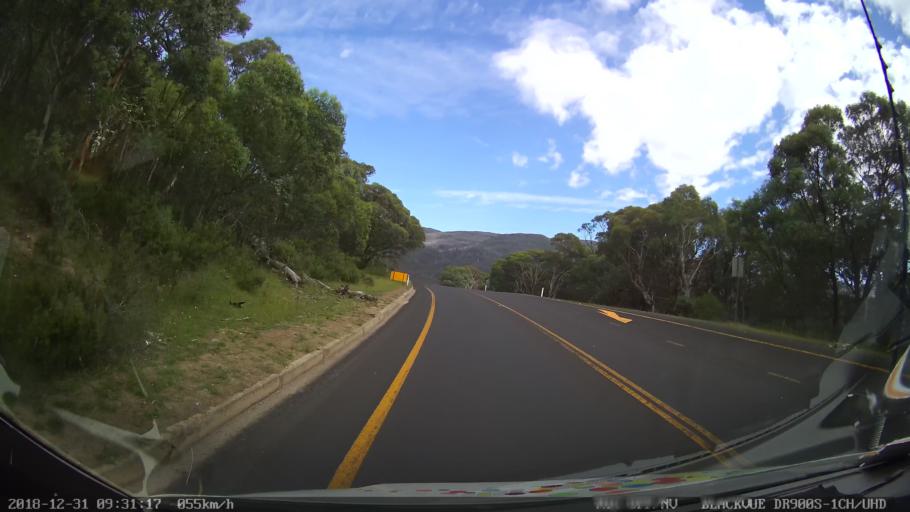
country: AU
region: New South Wales
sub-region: Snowy River
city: Jindabyne
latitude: -36.4499
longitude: 148.4443
